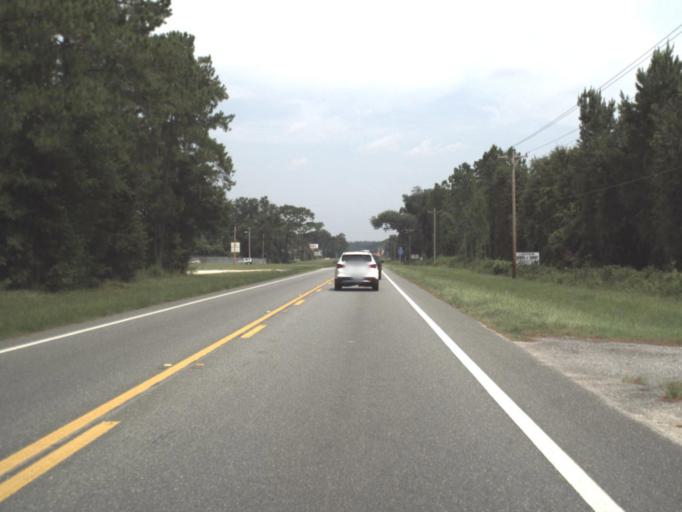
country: US
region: Florida
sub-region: Columbia County
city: Lake City
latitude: 30.1353
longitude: -82.6298
